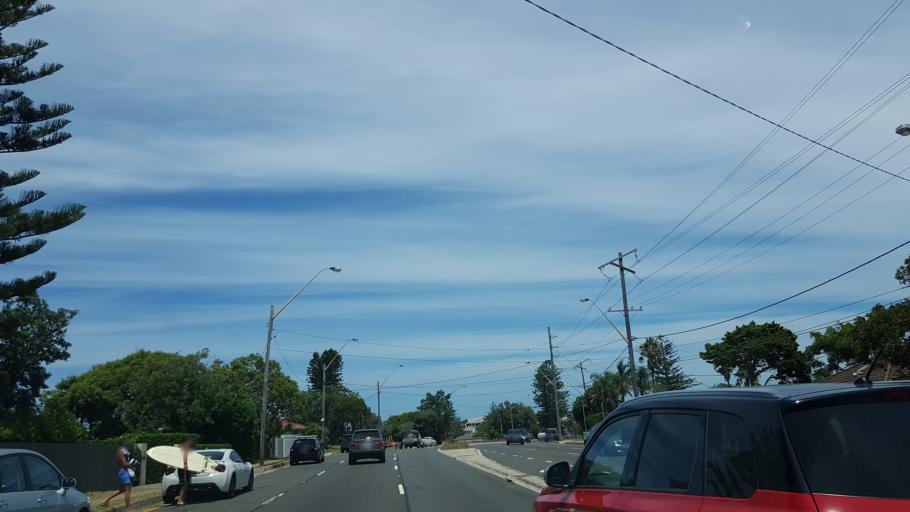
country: AU
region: New South Wales
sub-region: Pittwater
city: Newport
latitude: -33.6661
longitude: 151.3172
